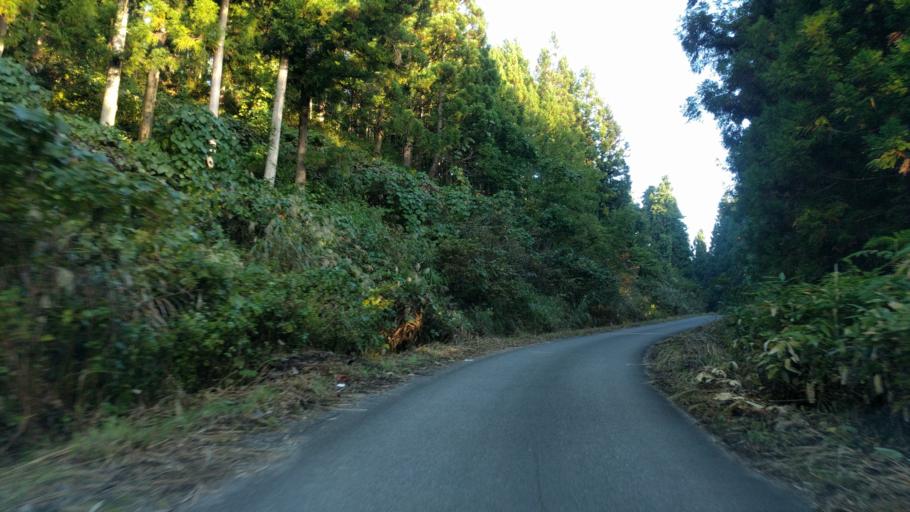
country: JP
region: Fukushima
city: Kitakata
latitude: 37.4292
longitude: 139.7924
